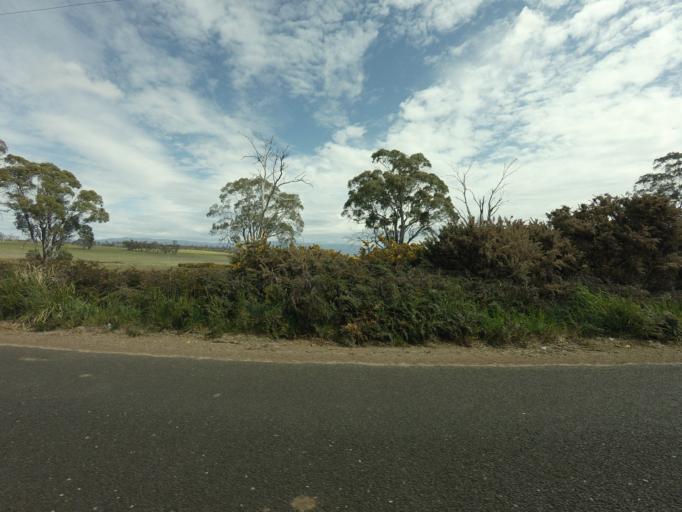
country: AU
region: Tasmania
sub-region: Northern Midlands
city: Longford
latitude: -41.7191
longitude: 147.1875
